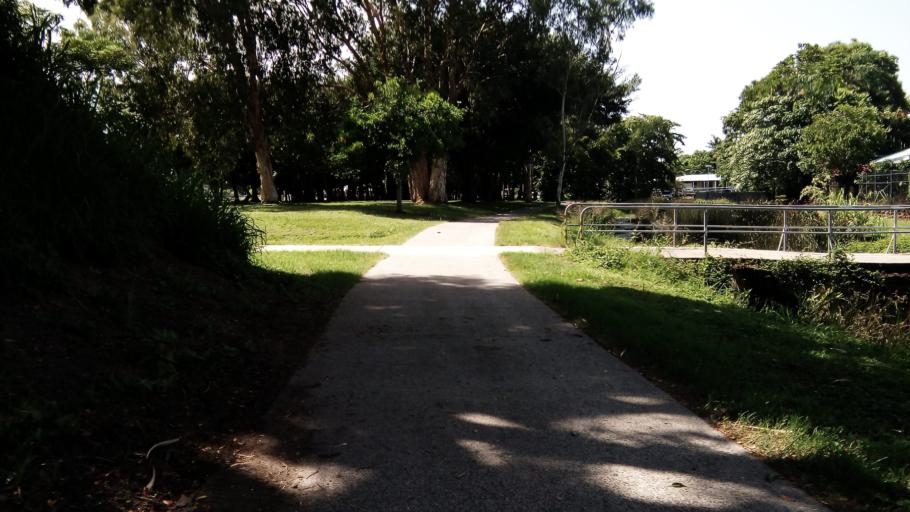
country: AU
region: Queensland
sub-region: Cairns
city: Cairns
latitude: -16.9136
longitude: 145.7612
